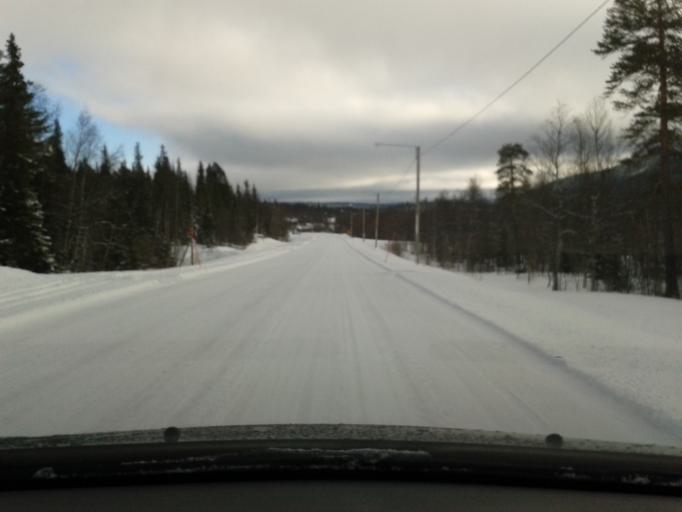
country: SE
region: Vaesterbotten
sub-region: Vilhelmina Kommun
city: Sjoberg
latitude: 65.2522
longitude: 15.5414
